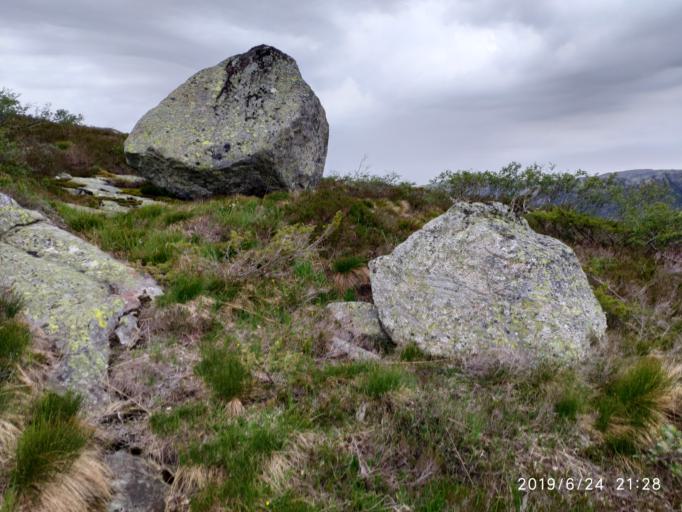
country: NO
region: Vest-Agder
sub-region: Sirdal
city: Tonstad
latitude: 58.7633
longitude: 6.7148
